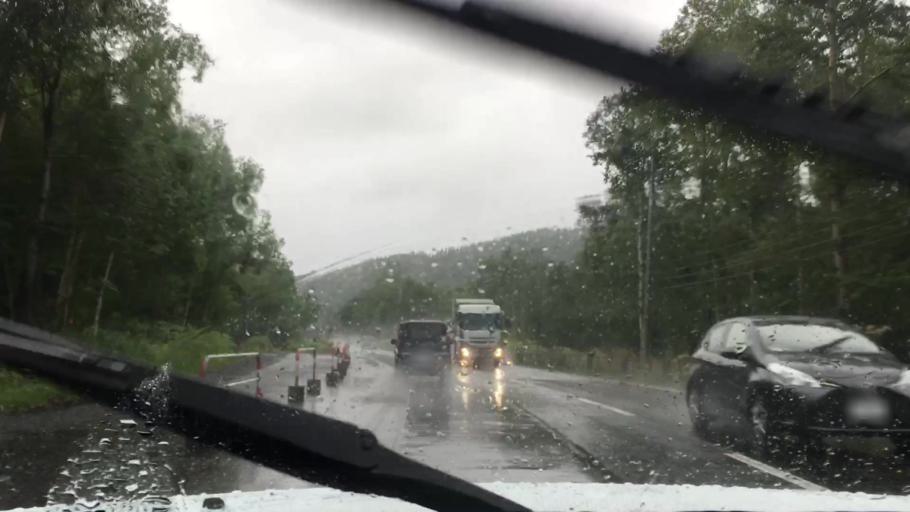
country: JP
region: Hokkaido
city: Otaru
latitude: 42.8436
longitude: 141.0161
